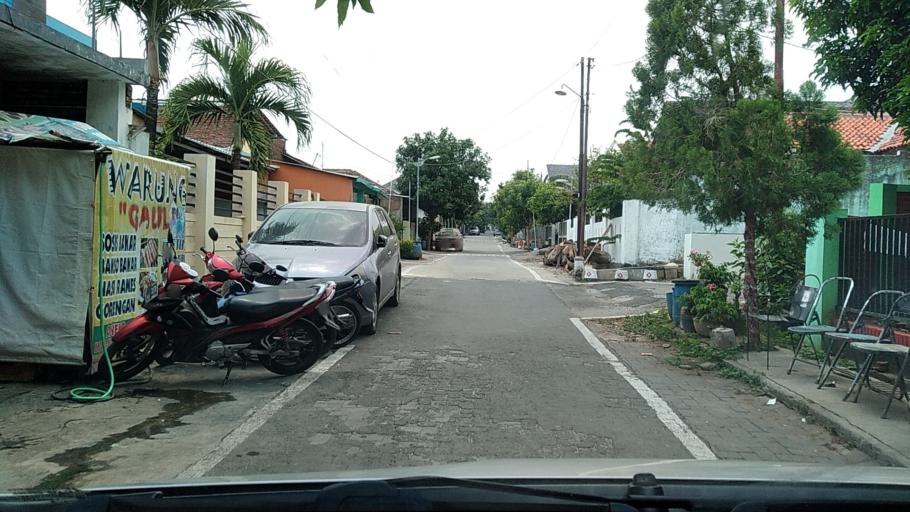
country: ID
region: Central Java
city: Semarang
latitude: -7.0119
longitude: 110.3728
